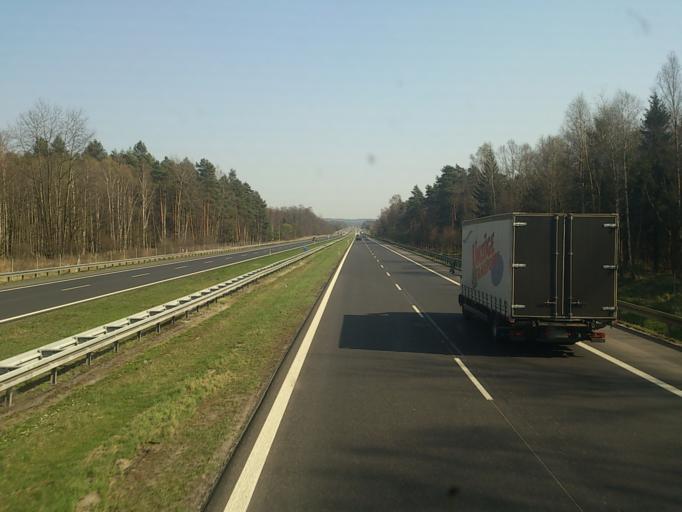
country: PL
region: Lesser Poland Voivodeship
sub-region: Powiat chrzanowski
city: Bolecin
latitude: 50.1318
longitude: 19.4774
